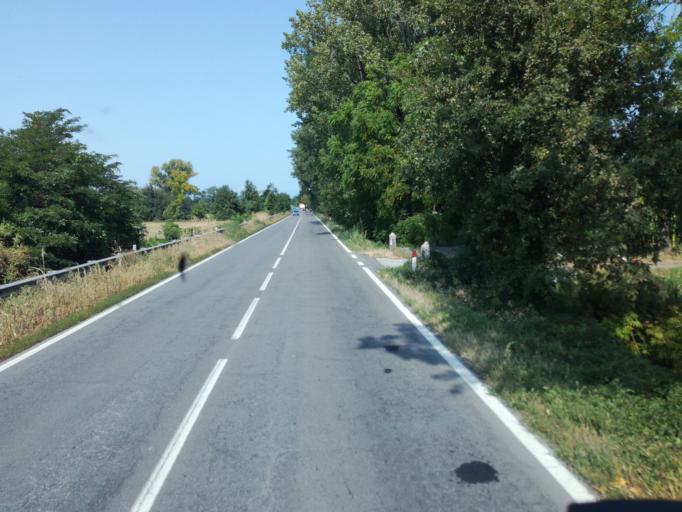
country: IT
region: Lombardy
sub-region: Provincia di Brescia
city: Barbariga
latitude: 45.3878
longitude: 10.0634
